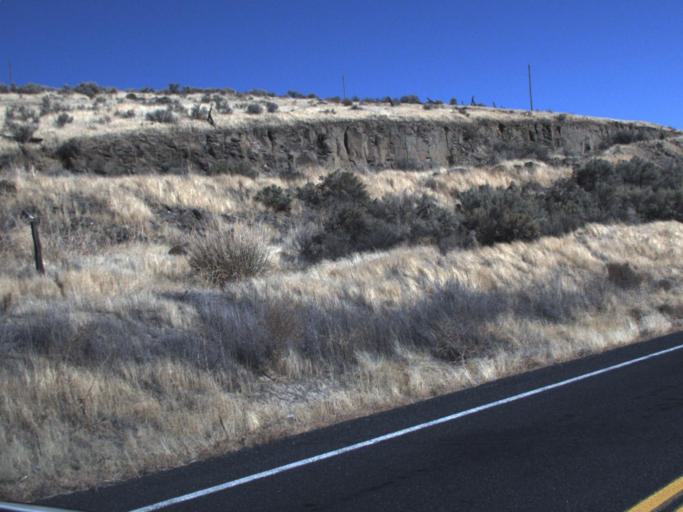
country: US
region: Washington
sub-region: Adams County
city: Ritzville
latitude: 46.9708
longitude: -118.6498
